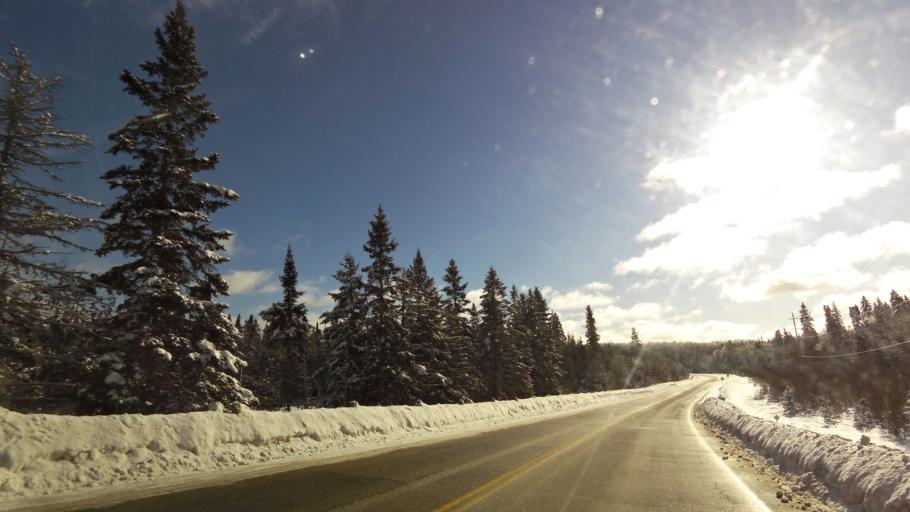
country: CA
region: Ontario
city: Bancroft
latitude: 44.9784
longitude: -78.2793
